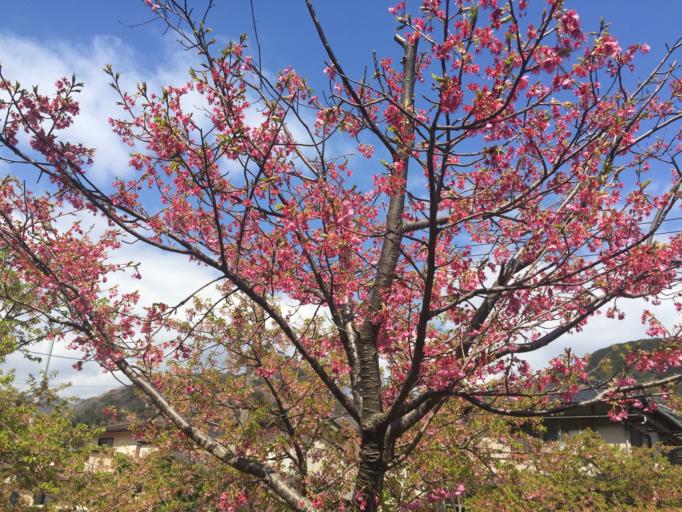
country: JP
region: Shizuoka
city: Shimoda
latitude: 34.7450
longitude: 138.9955
